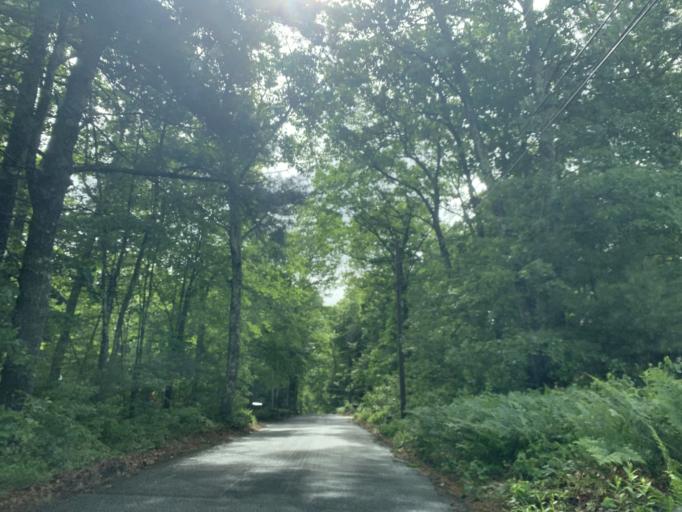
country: US
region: Massachusetts
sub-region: Worcester County
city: Upton
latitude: 42.2016
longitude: -71.6366
